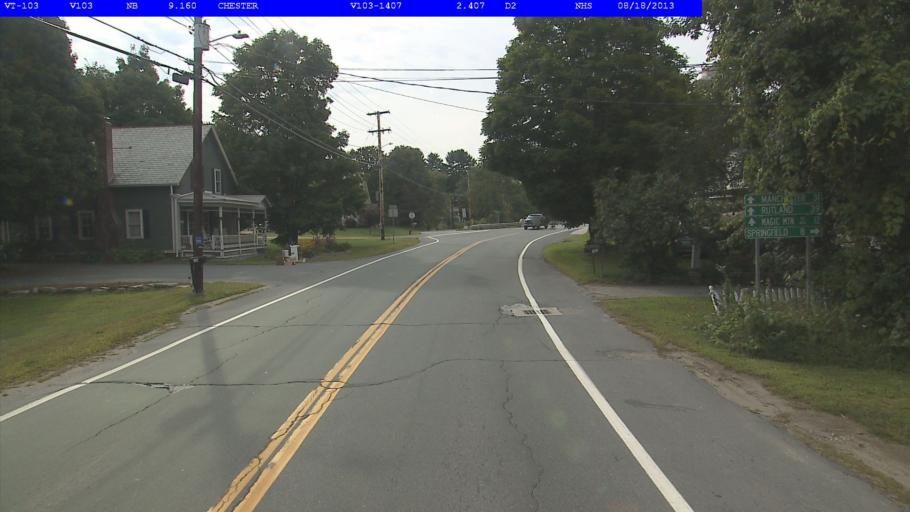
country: US
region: Vermont
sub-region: Windsor County
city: Chester
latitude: 43.2576
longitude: -72.5868
